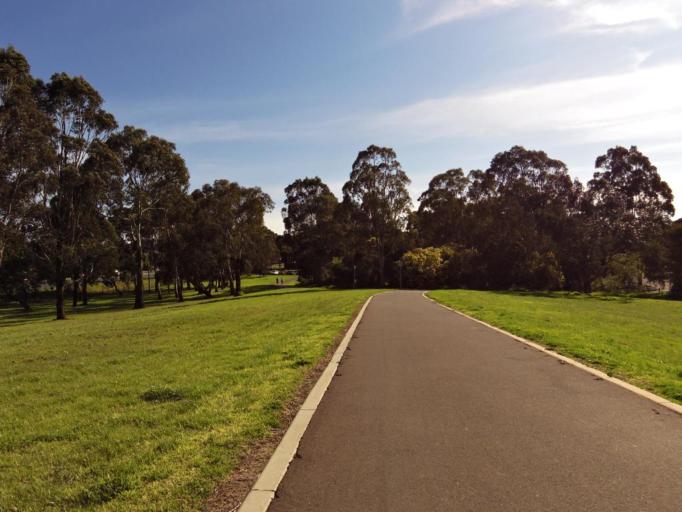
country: AU
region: Victoria
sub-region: Monash
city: Mulgrave
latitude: -37.9074
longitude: 145.2017
